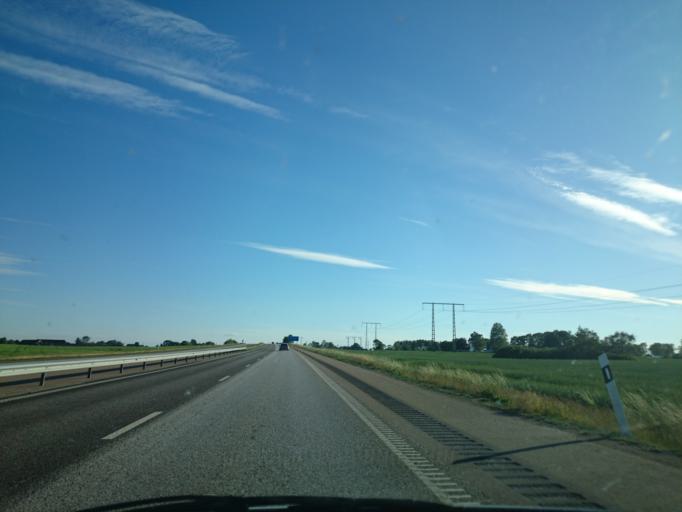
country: SE
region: Skane
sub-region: Astorps Kommun
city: Astorp
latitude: 56.1543
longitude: 12.9493
